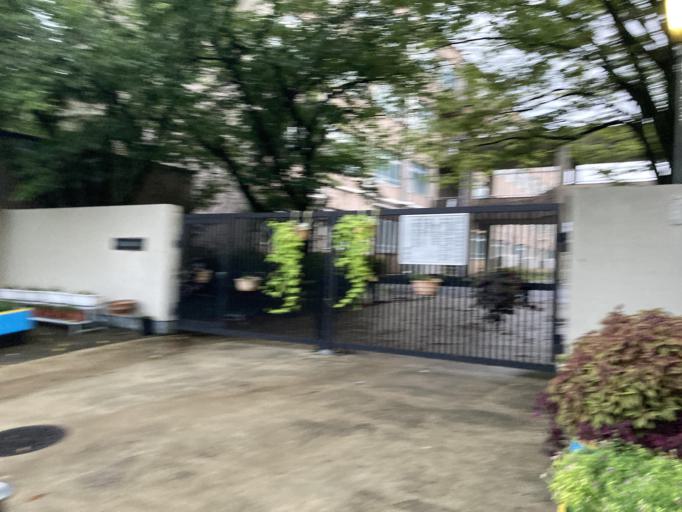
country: JP
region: Kyoto
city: Kyoto
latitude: 34.9822
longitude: 135.8038
